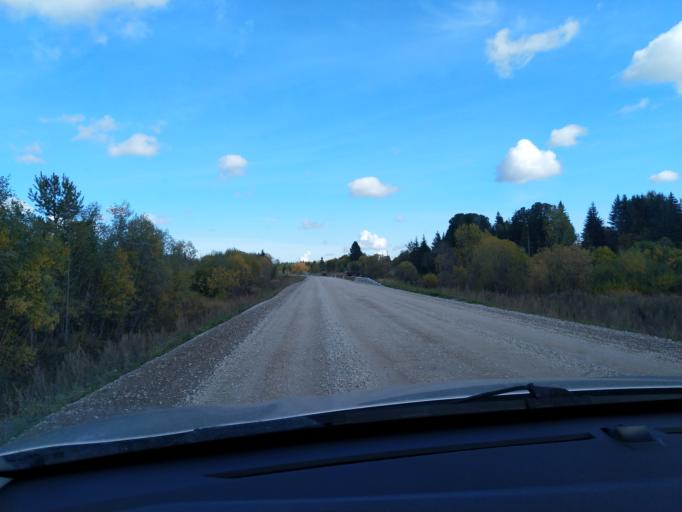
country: RU
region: Perm
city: Usol'ye
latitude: 59.4613
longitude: 56.3598
